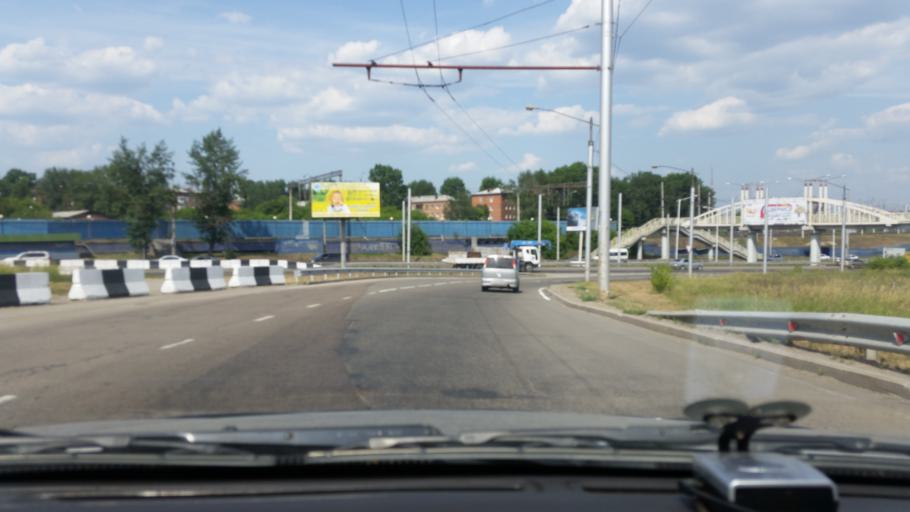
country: RU
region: Irkutsk
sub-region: Irkutskiy Rayon
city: Irkutsk
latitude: 52.2538
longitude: 104.2652
